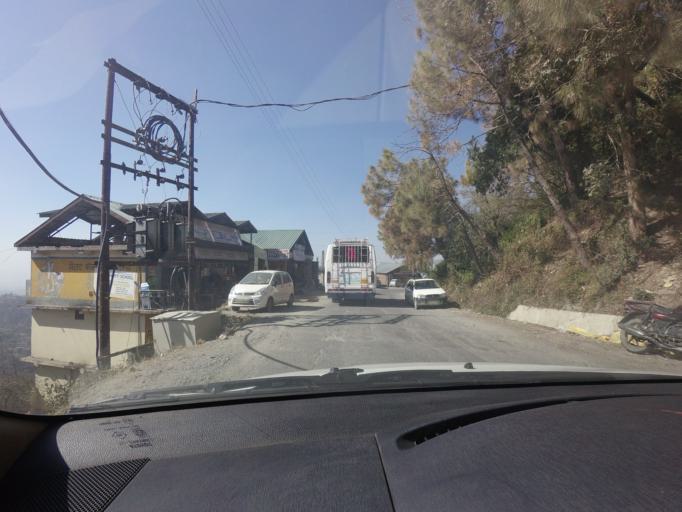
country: IN
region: Himachal Pradesh
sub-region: Shimla
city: Jutogh
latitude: 31.1354
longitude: 77.0873
